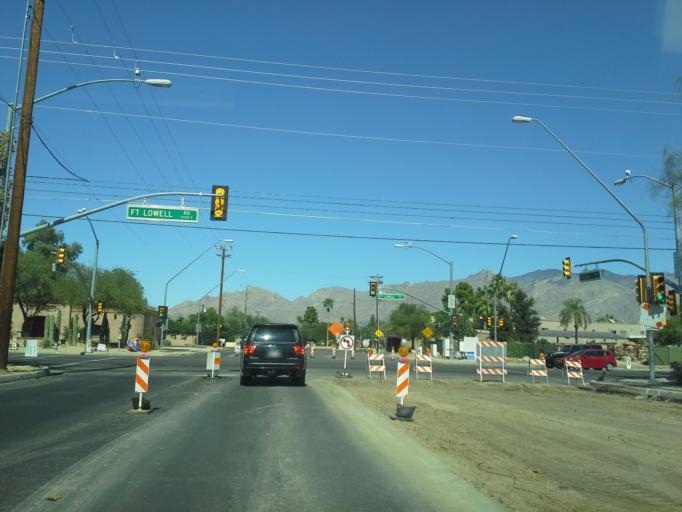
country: US
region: Arizona
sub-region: Pima County
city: Catalina Foothills
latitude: 32.2645
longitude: -110.9353
